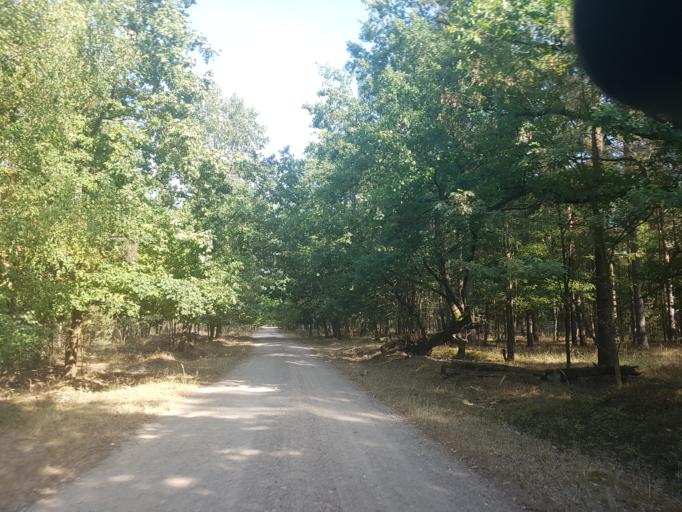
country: DE
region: Saxony-Anhalt
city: Jessen
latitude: 51.8696
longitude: 13.0048
